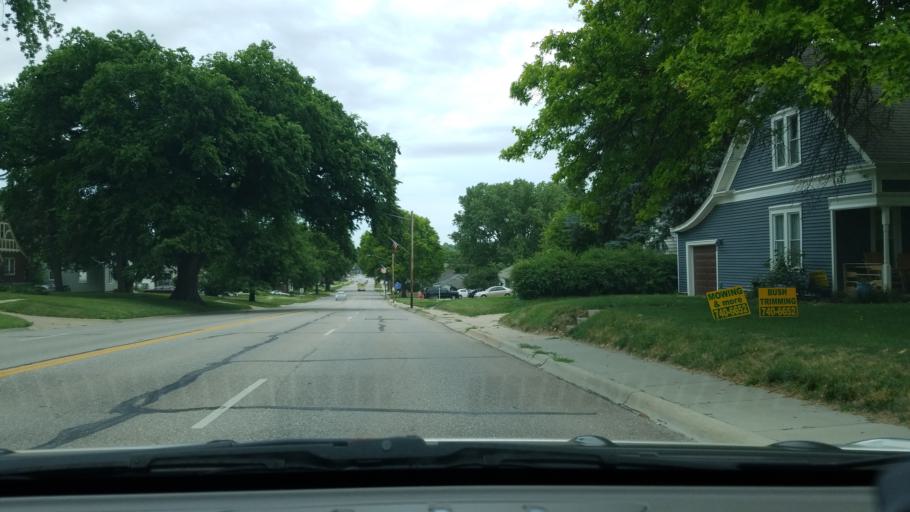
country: US
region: Nebraska
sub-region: Sarpy County
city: Papillion
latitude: 41.1487
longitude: -96.0429
